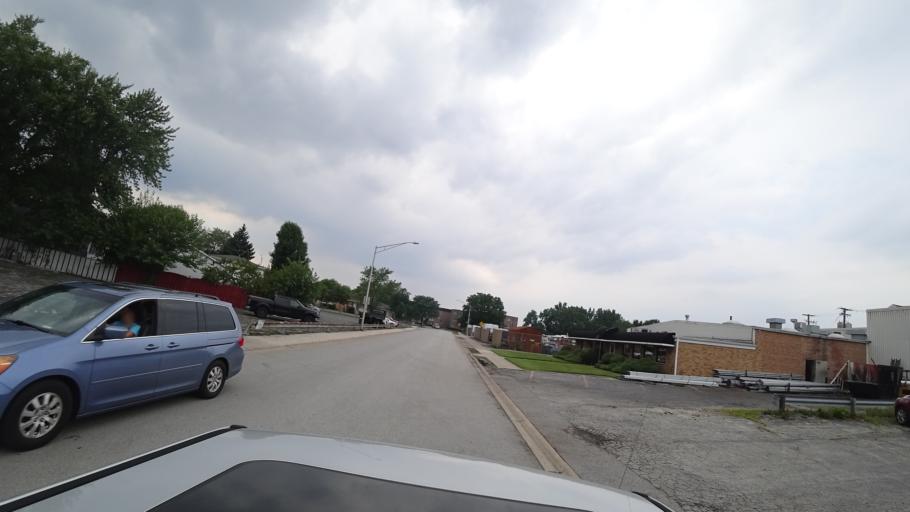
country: US
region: Illinois
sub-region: Cook County
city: Oak Lawn
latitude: 41.6953
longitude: -87.7609
